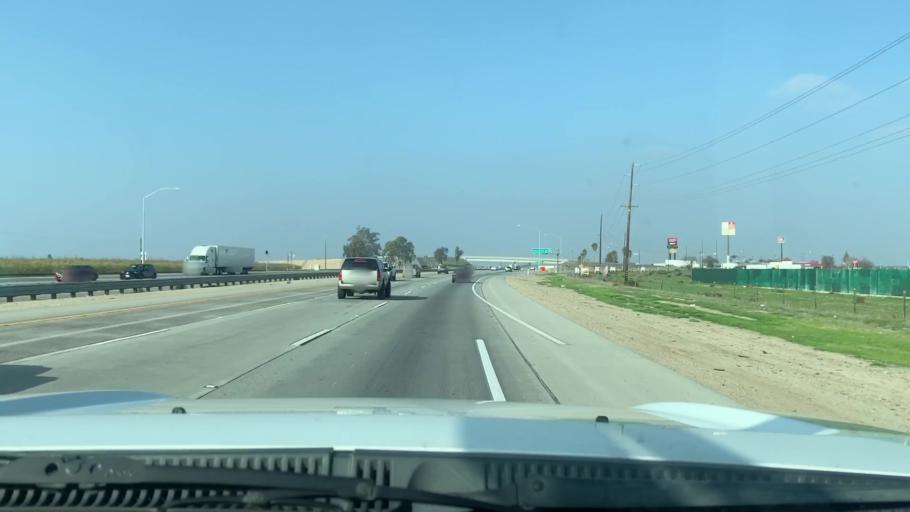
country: US
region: California
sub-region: Kern County
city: Shafter
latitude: 35.5249
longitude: -119.1878
